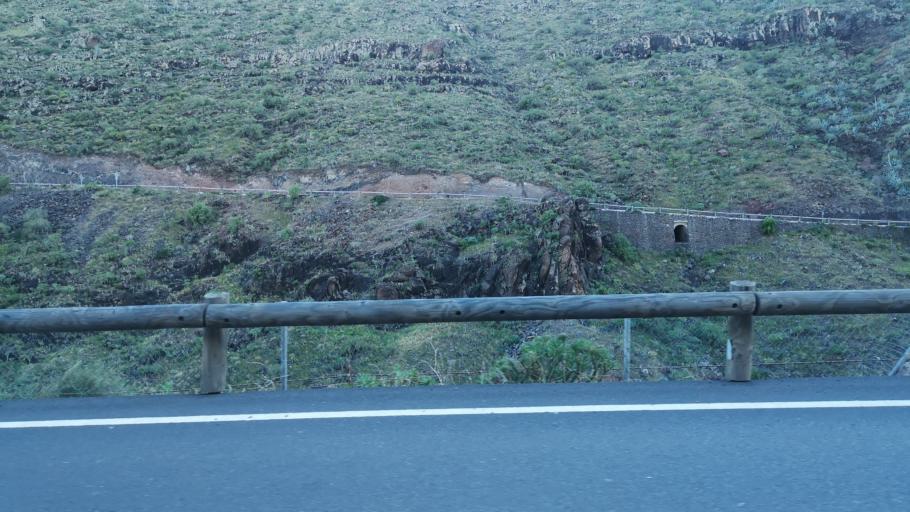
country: ES
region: Canary Islands
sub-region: Provincia de Santa Cruz de Tenerife
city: San Sebastian de la Gomera
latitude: 28.0870
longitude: -17.1293
